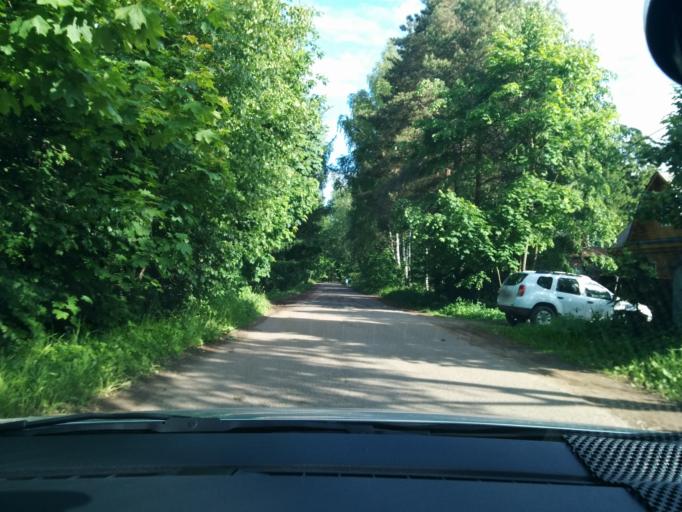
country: RU
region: Moskovskaya
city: Lugovaya
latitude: 56.0518
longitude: 37.4883
